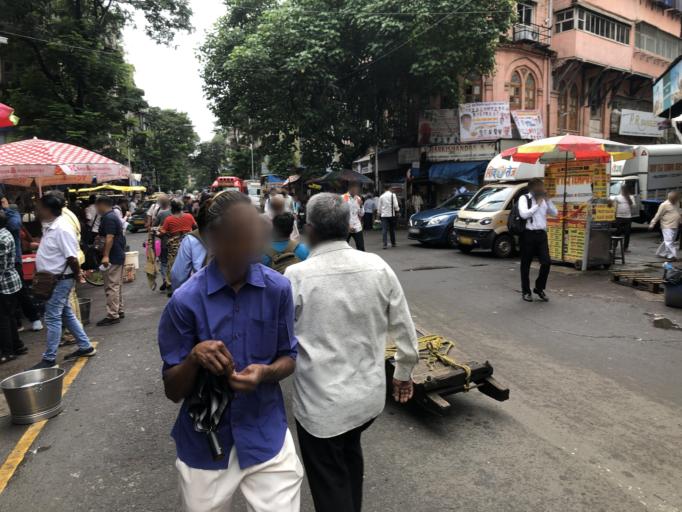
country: IN
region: Maharashtra
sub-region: Raigarh
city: Uran
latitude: 18.9486
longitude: 72.8317
